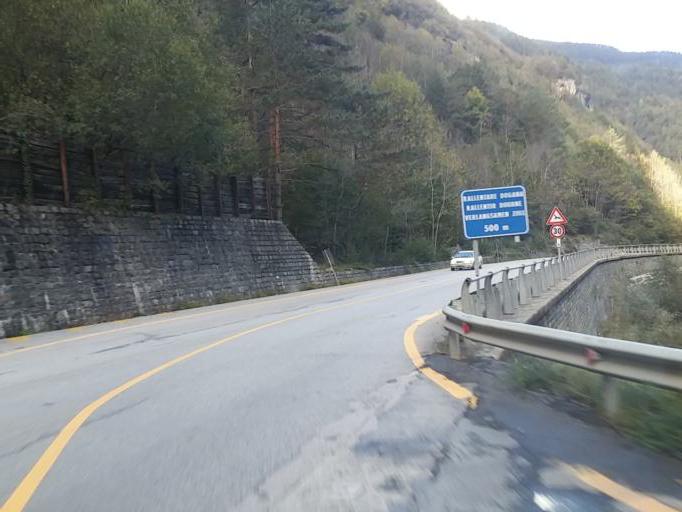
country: IT
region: Piedmont
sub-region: Provincia Verbano-Cusio-Ossola
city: Trasquera
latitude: 46.2038
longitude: 8.1855
